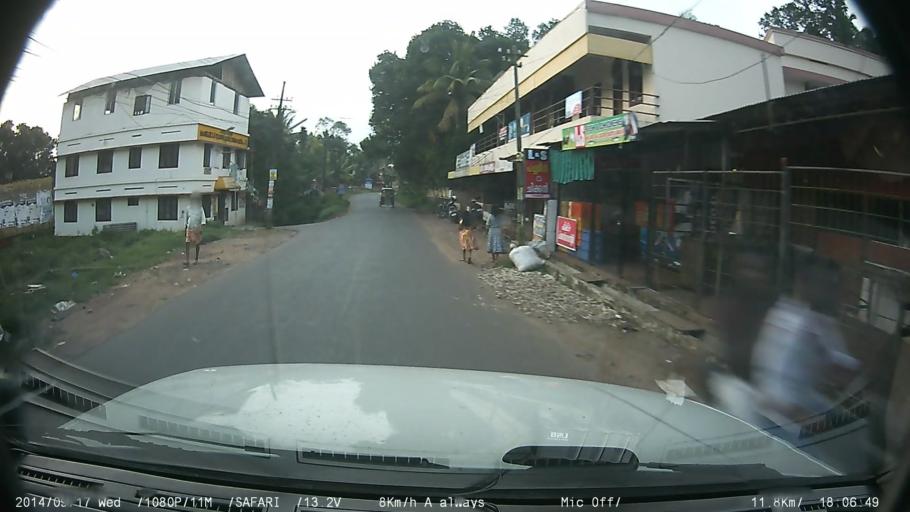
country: IN
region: Kerala
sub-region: Kottayam
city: Changanacheri
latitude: 9.4258
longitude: 76.5619
